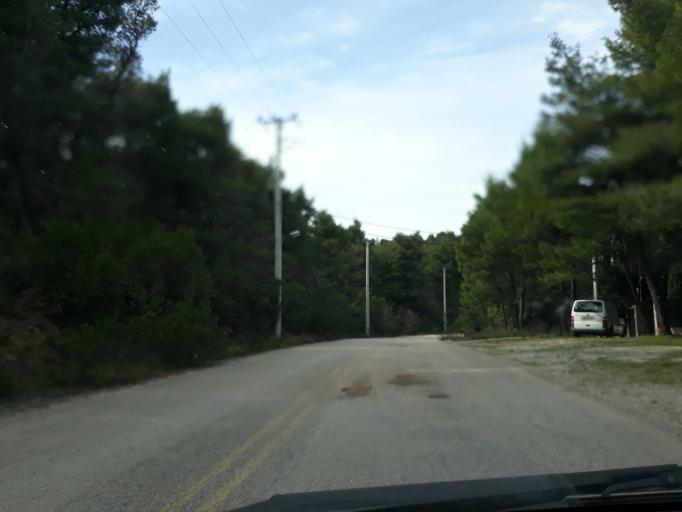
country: GR
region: Attica
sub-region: Nomarchia Anatolikis Attikis
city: Afidnes
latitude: 38.1977
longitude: 23.7920
